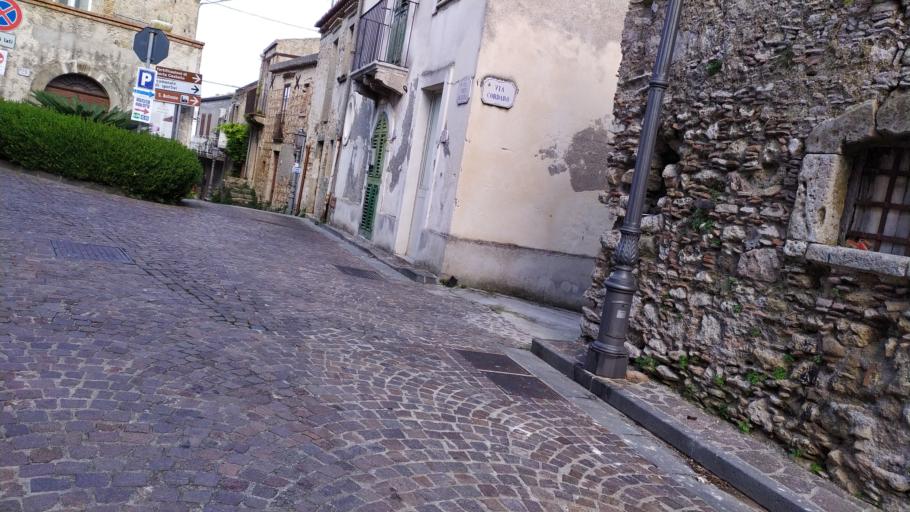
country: IT
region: Sicily
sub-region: Messina
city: Rometta
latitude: 38.1718
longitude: 15.4158
